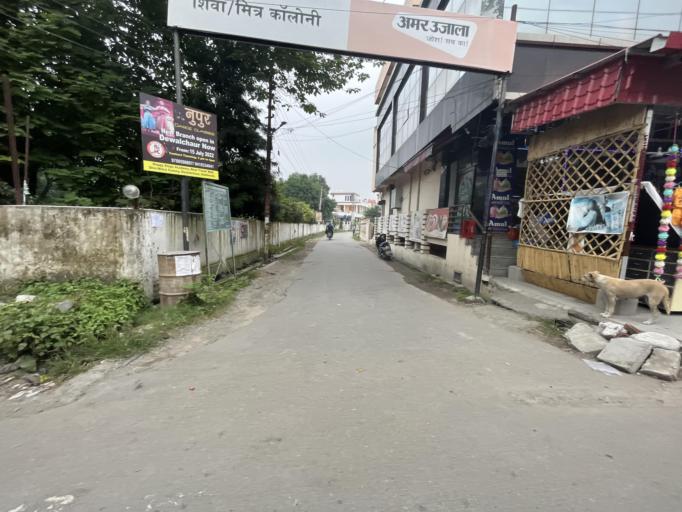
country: IN
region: Uttarakhand
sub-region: Naini Tal
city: Haldwani
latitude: 29.1942
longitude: 79.5085
